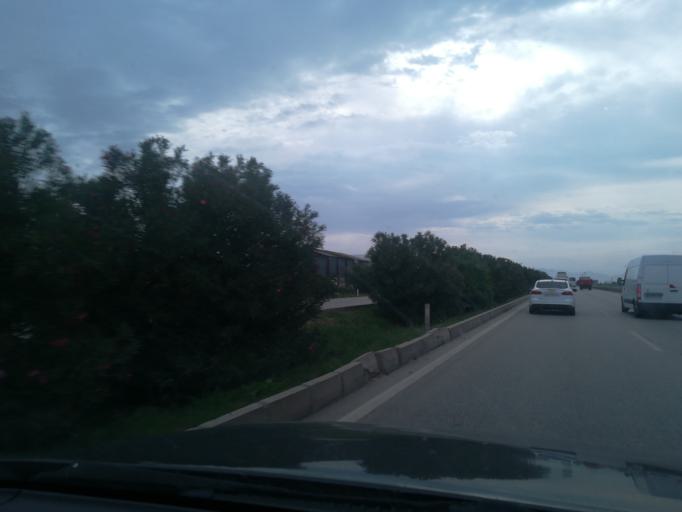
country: TR
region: Adana
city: Yakapinar
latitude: 36.9719
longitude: 35.5160
